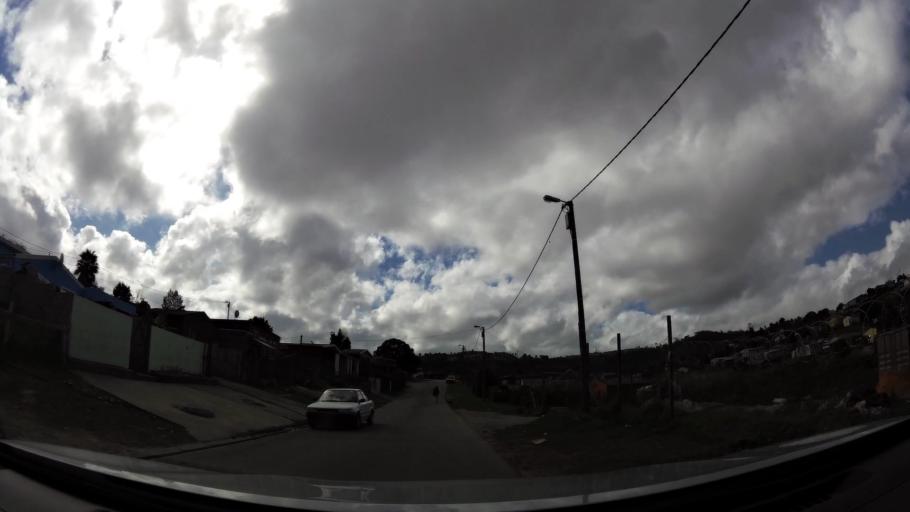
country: ZA
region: Western Cape
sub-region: Eden District Municipality
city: Knysna
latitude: -34.0519
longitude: 23.0921
